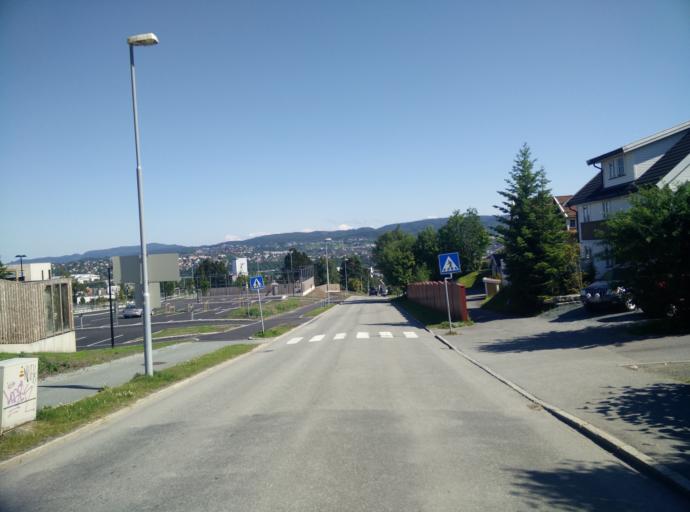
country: NO
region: Sor-Trondelag
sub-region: Trondheim
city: Trondheim
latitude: 63.4146
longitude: 10.3680
